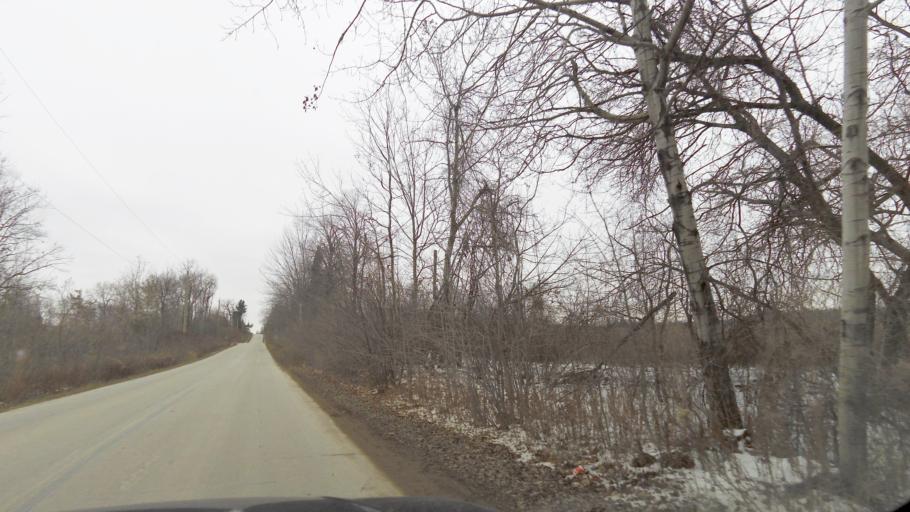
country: CA
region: Ontario
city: Vaughan
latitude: 43.8530
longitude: -79.6145
